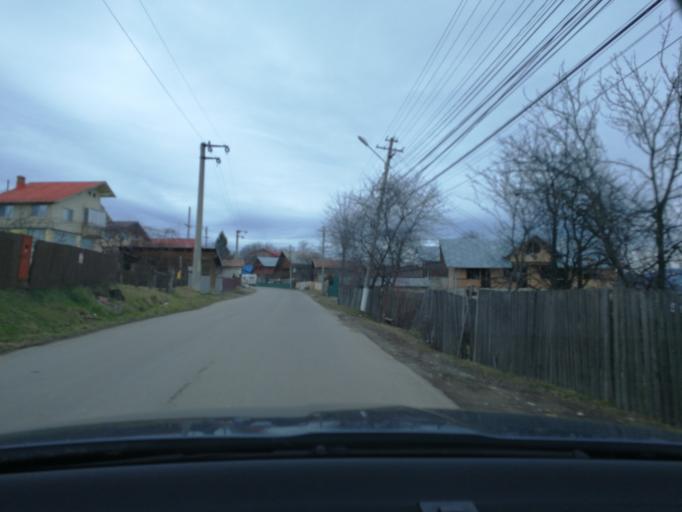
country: RO
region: Prahova
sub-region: Oras Breaza
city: Breaza
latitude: 45.1806
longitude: 25.6551
